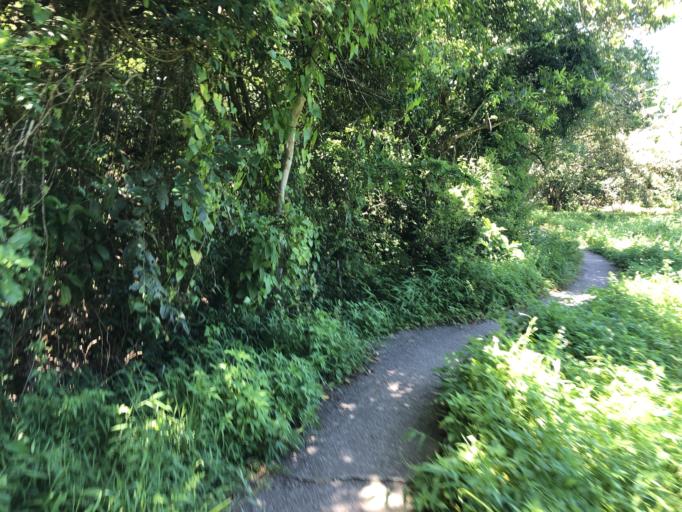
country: HK
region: Tuen Mun
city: Tuen Mun
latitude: 22.2792
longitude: 113.9884
